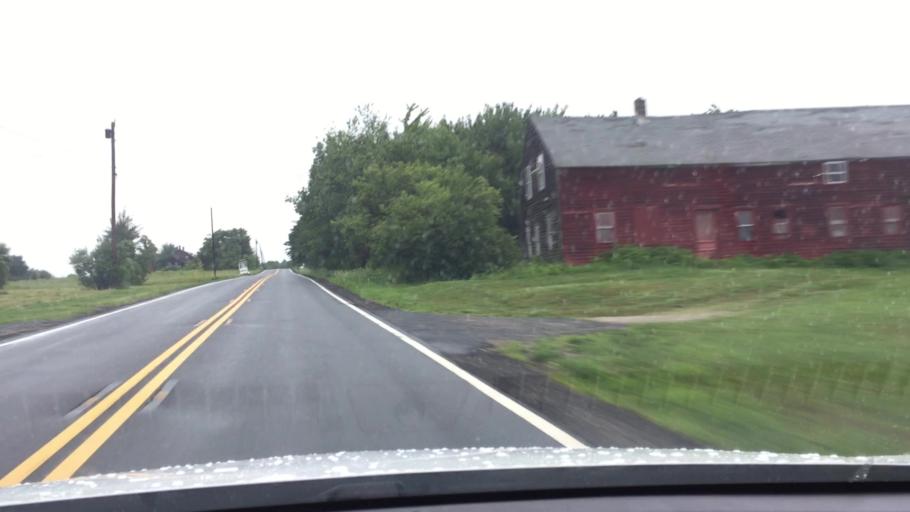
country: US
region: Massachusetts
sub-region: Berkshire County
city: Becket
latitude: 42.3635
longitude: -73.1406
